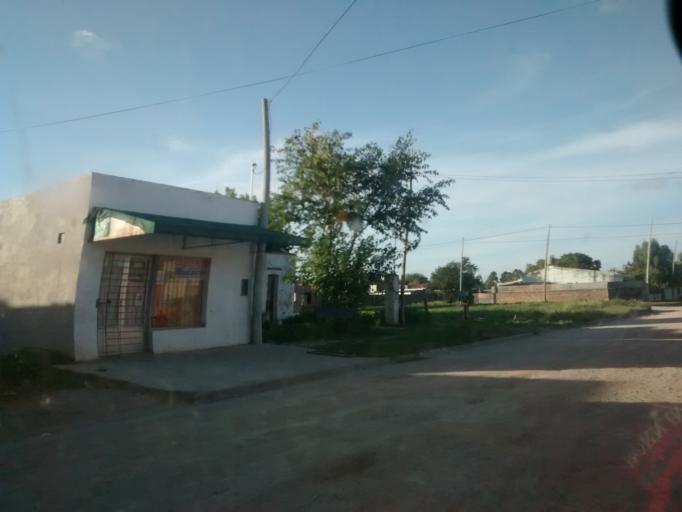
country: AR
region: Buenos Aires
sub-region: Partido de Loberia
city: Loberia
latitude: -38.1721
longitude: -58.7751
